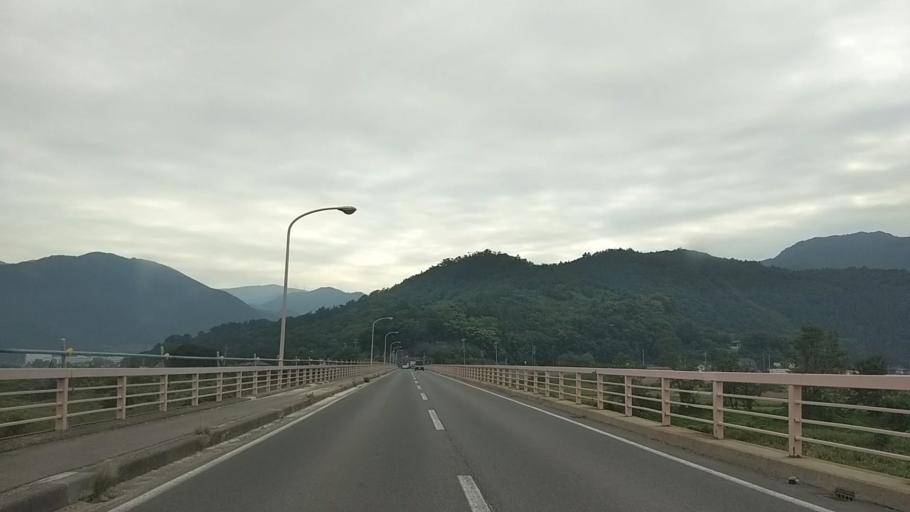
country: JP
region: Nagano
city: Nagano-shi
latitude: 36.6066
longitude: 138.2225
